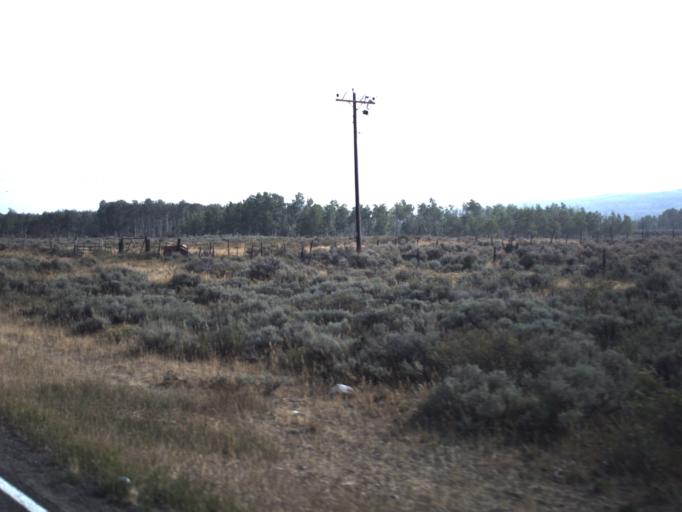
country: US
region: Wyoming
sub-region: Uinta County
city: Evanston
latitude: 40.9690
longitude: -110.8485
